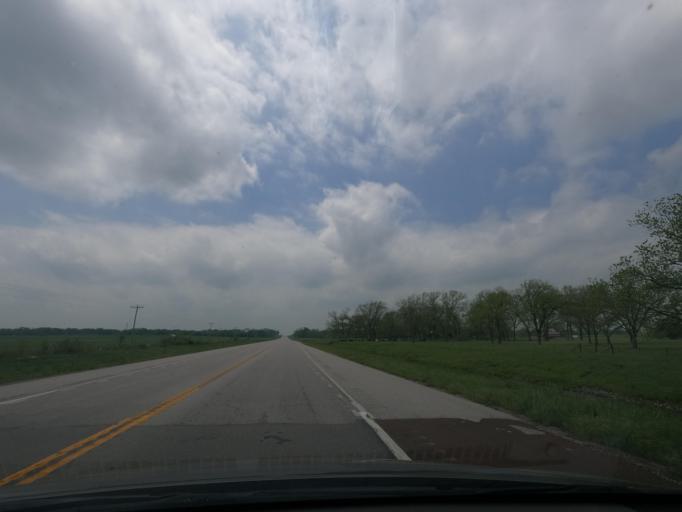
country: US
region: Kansas
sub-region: Labette County
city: Parsons
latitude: 37.3402
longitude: -95.1370
